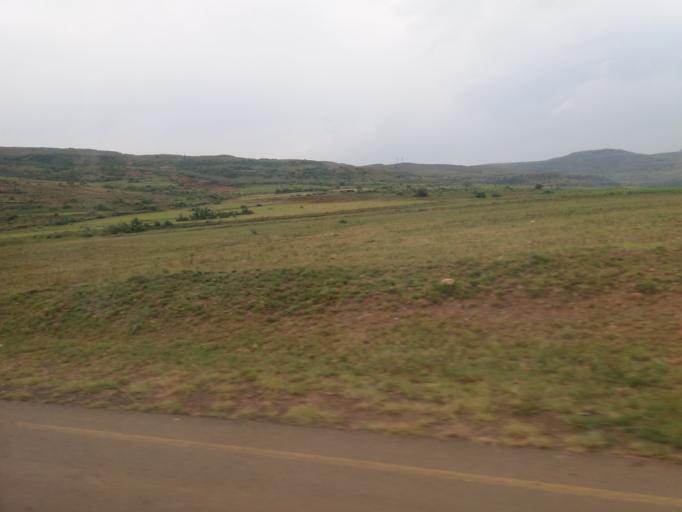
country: LS
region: Berea
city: Teyateyaneng
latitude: -29.3241
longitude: 27.7641
